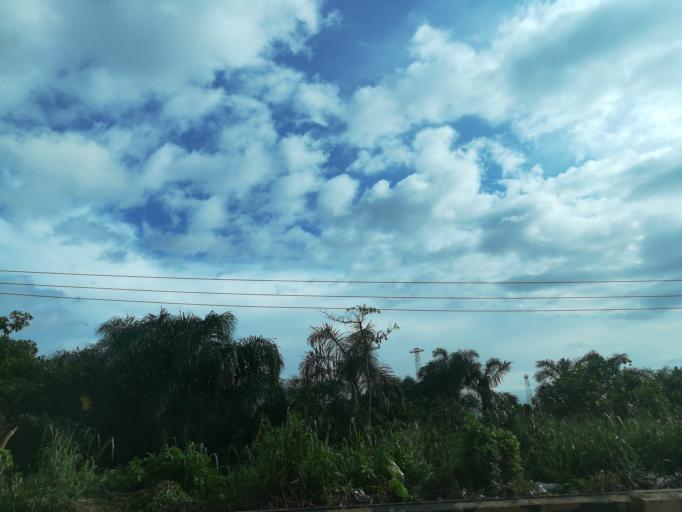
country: NG
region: Lagos
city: Ebute Ikorodu
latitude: 6.5981
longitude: 3.4977
